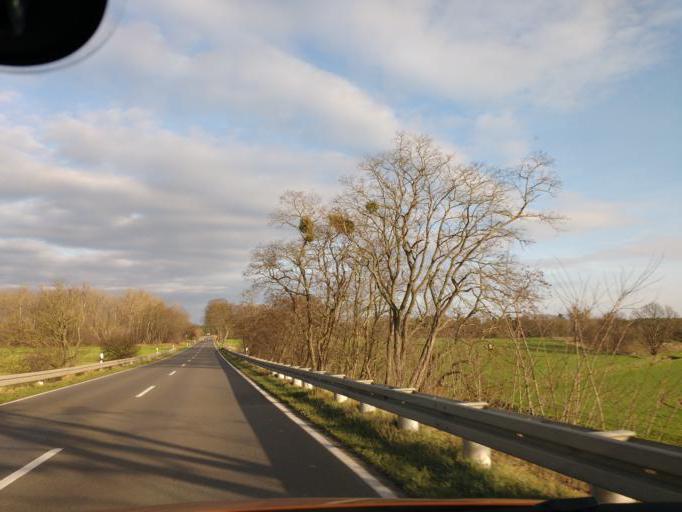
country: DE
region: Brandenburg
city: Wriezen
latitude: 52.7005
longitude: 14.1149
